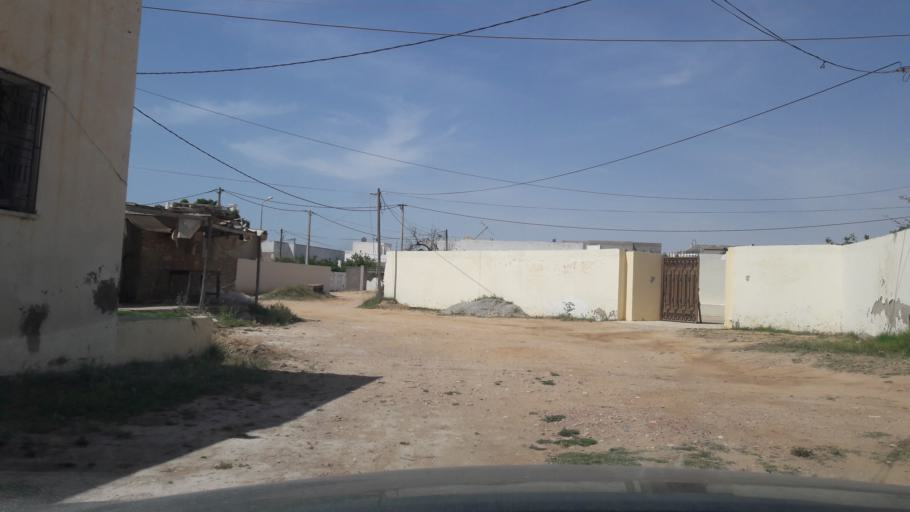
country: TN
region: Safaqis
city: Al Qarmadah
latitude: 34.7897
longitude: 10.7551
